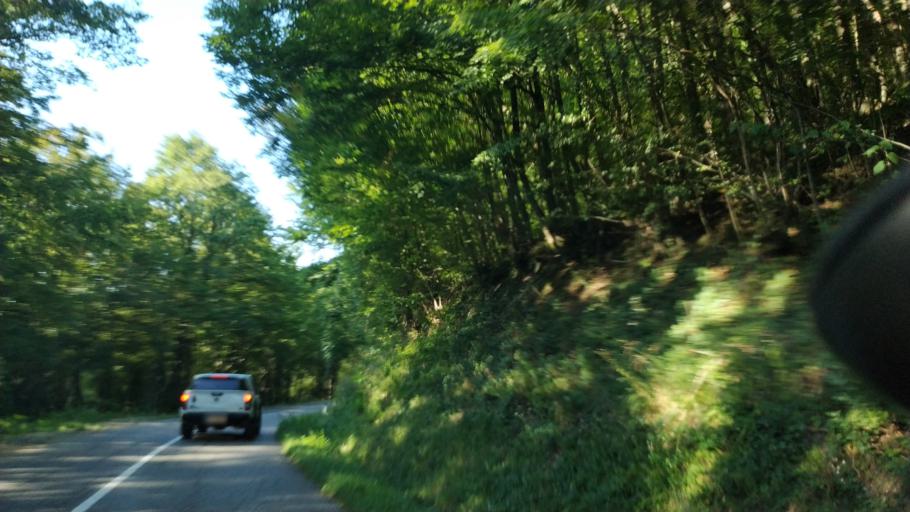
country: RS
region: Central Serbia
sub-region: Rasinski Okrug
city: Krusevac
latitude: 43.4666
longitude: 21.3596
